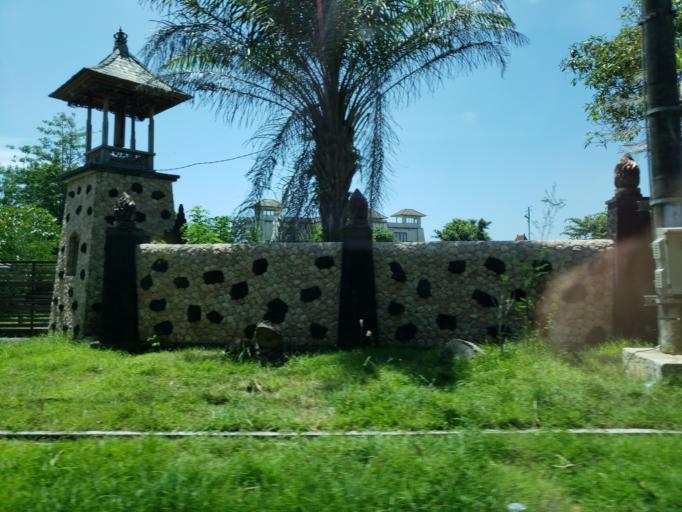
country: ID
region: Bali
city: Kangin
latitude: -8.8396
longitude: 115.1380
